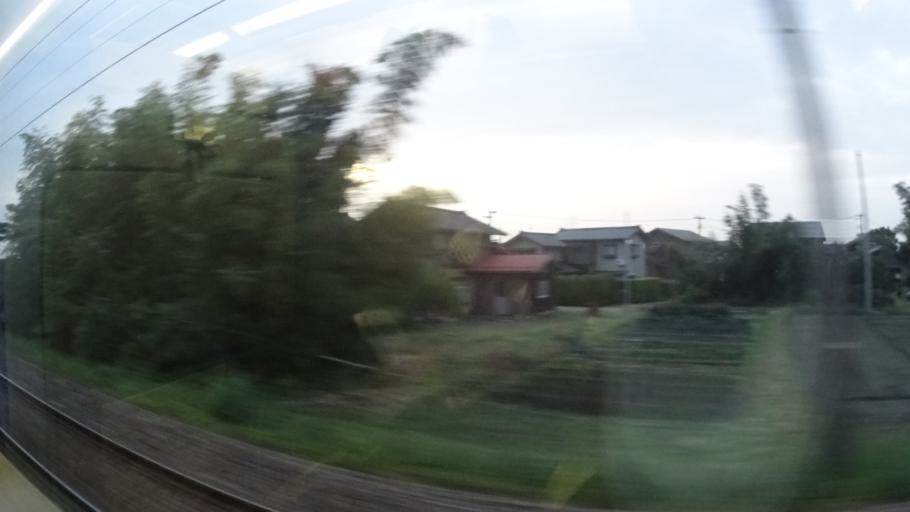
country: JP
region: Niigata
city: Shibata
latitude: 38.0831
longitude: 139.4203
